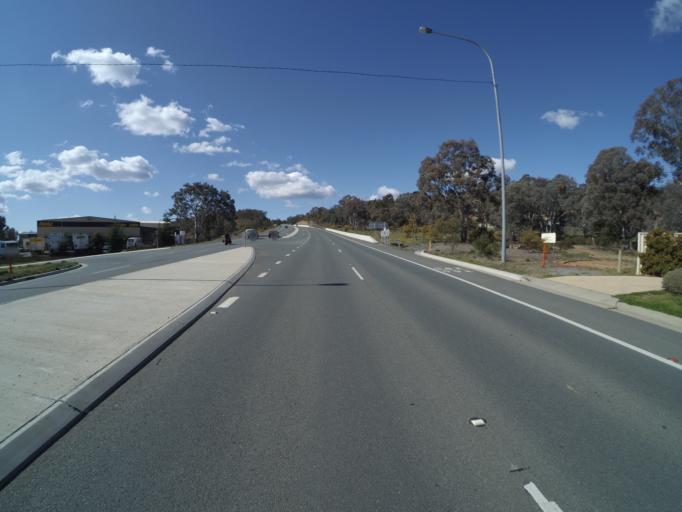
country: AU
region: New South Wales
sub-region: Queanbeyan
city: Queanbeyan
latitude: -35.3451
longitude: 149.2494
